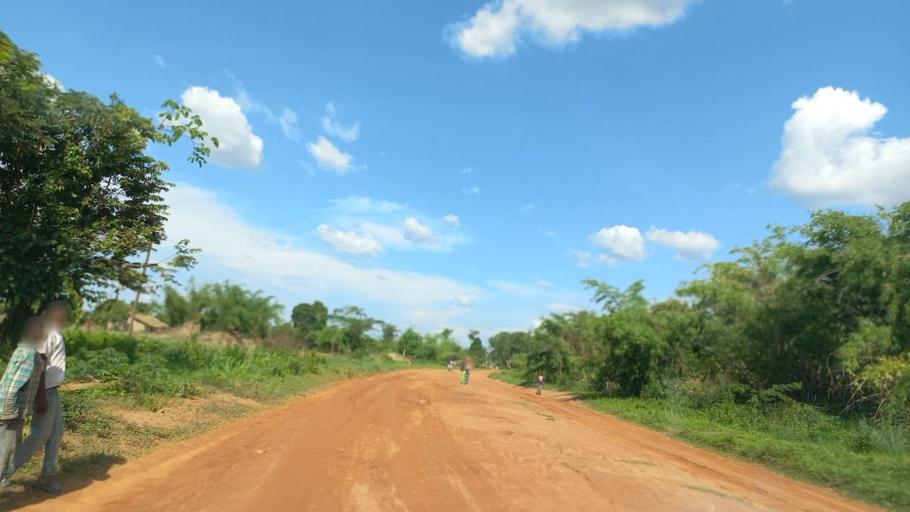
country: ZM
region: Copperbelt
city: Kitwe
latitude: -12.8651
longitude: 28.3729
